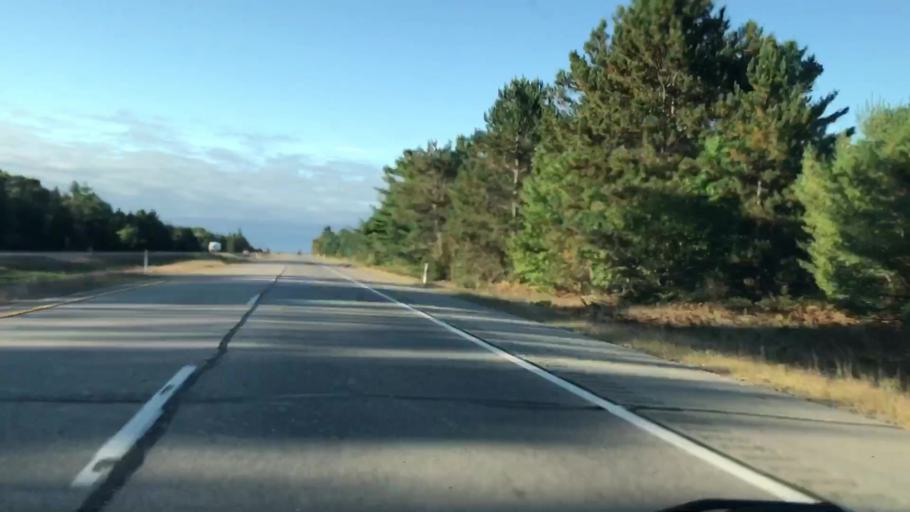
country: US
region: Michigan
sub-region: Chippewa County
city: Sault Ste. Marie
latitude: 46.4324
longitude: -84.3902
